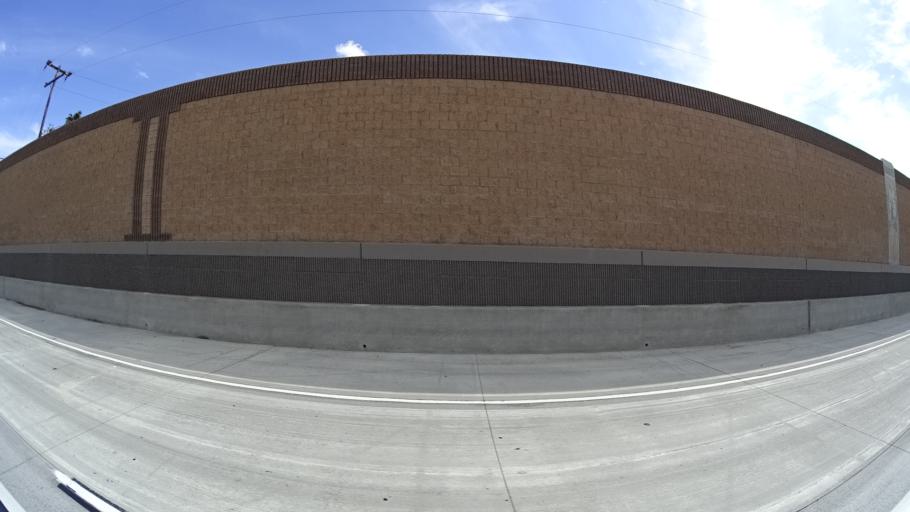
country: US
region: California
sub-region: Riverside County
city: Corona
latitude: 33.8813
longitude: -117.5952
